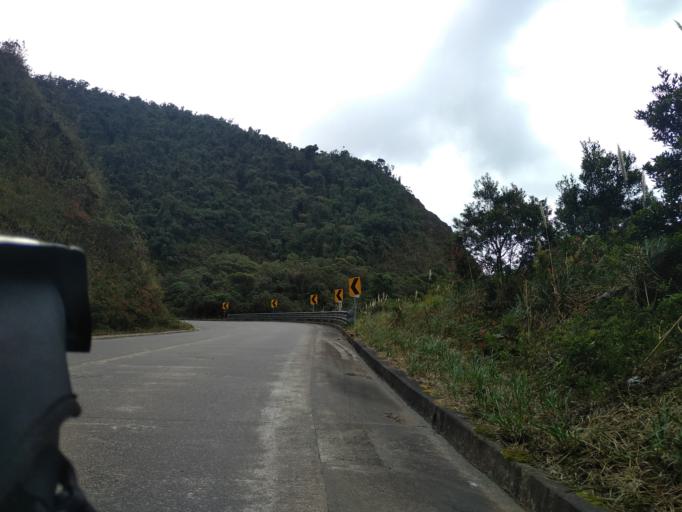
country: EC
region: Zamora-Chinchipe
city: Zamora
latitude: -4.4304
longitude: -79.1496
